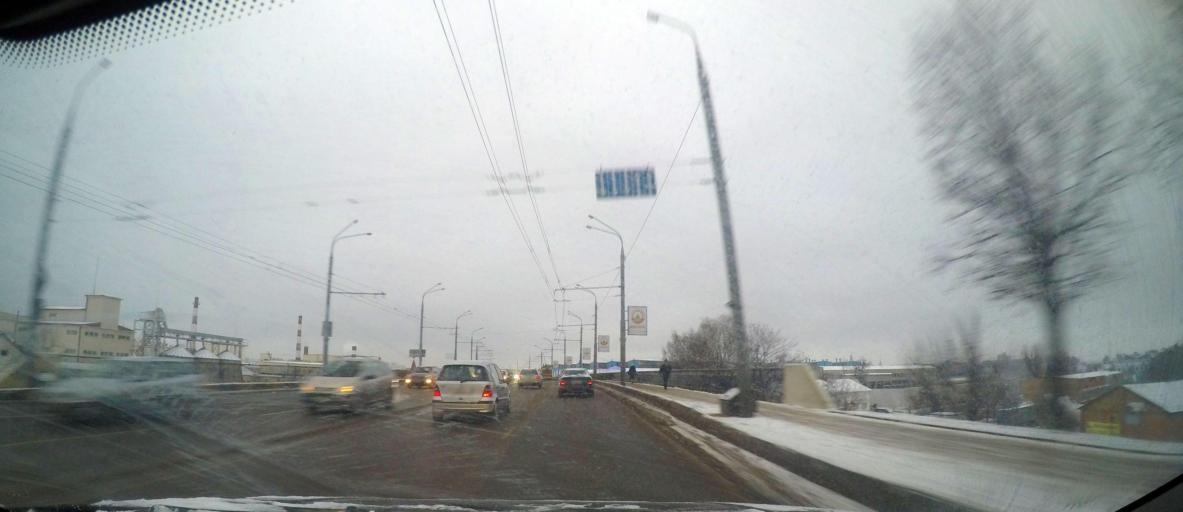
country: BY
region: Grodnenskaya
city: Hrodna
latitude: 53.6636
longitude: 23.8300
